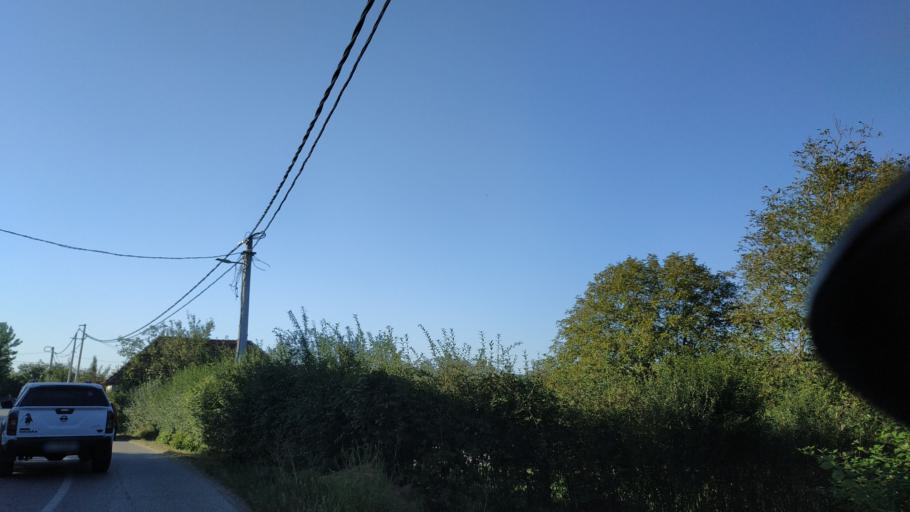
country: RS
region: Central Serbia
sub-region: Rasinski Okrug
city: Krusevac
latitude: 43.4911
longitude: 21.3457
